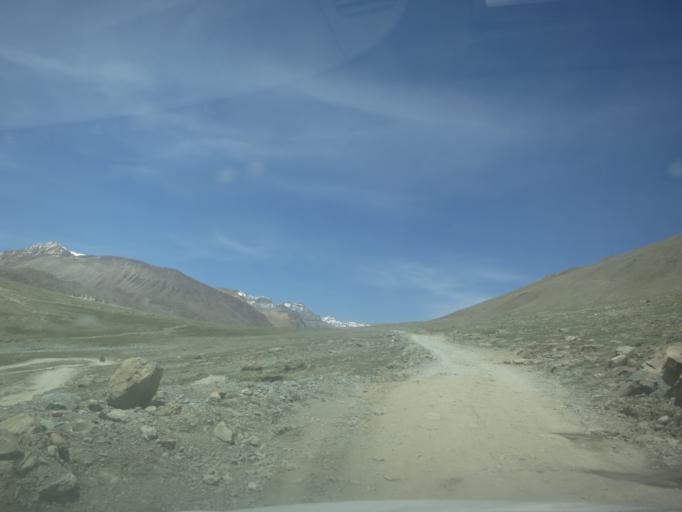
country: IN
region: Himachal Pradesh
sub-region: Kulu
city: Manali
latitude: 32.3888
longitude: 77.6307
